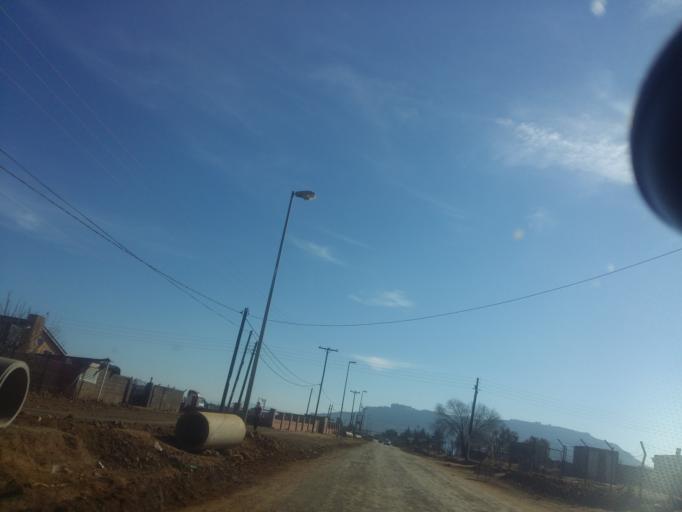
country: LS
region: Maseru
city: Maseru
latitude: -29.3692
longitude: 27.5237
